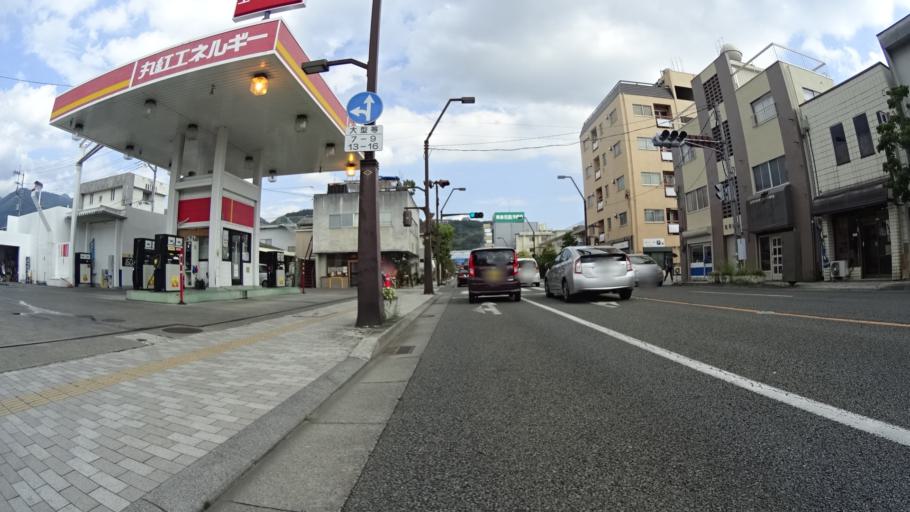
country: JP
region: Yamanashi
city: Kofu-shi
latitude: 35.6729
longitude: 138.5688
